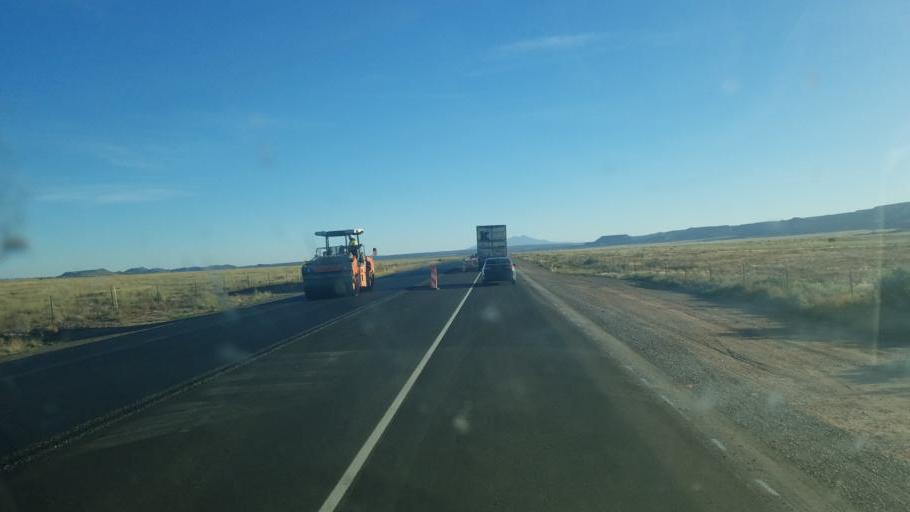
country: US
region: New Mexico
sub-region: Valencia County
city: Los Lunas
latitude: 34.8641
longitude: -107.0532
